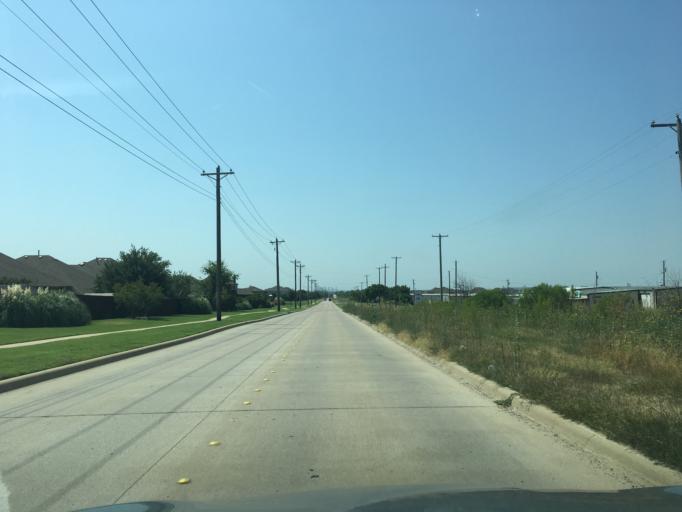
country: US
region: Texas
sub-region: Tarrant County
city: Haslet
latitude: 32.9226
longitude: -97.3315
